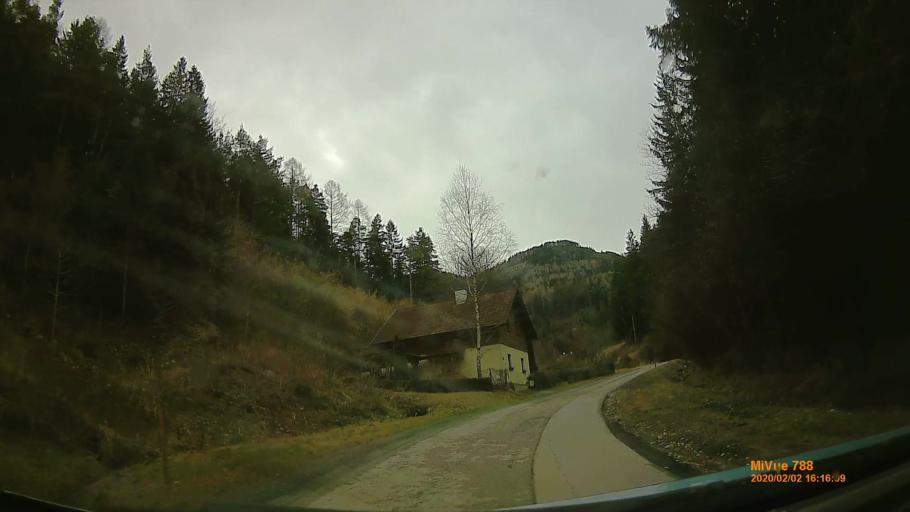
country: AT
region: Lower Austria
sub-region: Politischer Bezirk Neunkirchen
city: Semmering
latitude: 47.6535
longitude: 15.8160
